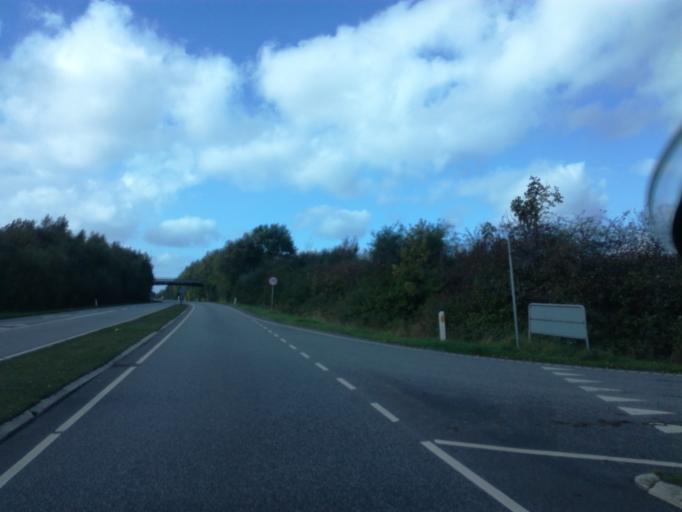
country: DK
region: South Denmark
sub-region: Fredericia Kommune
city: Fredericia
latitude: 55.6245
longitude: 9.7335
